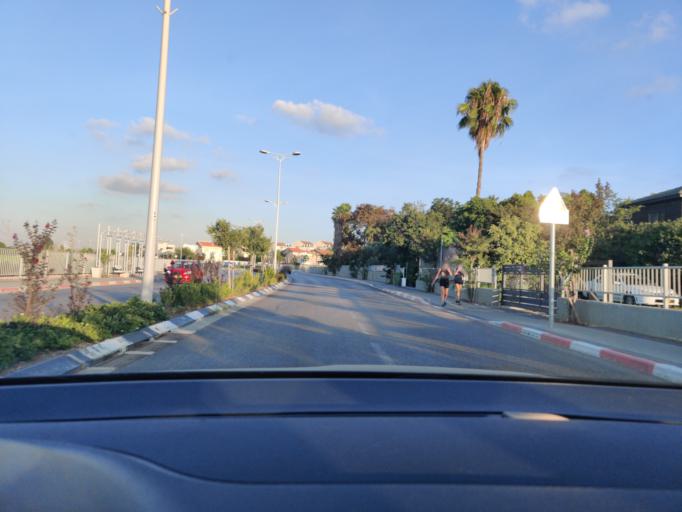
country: IL
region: Central District
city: Elyakhin
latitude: 32.4382
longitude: 34.9394
